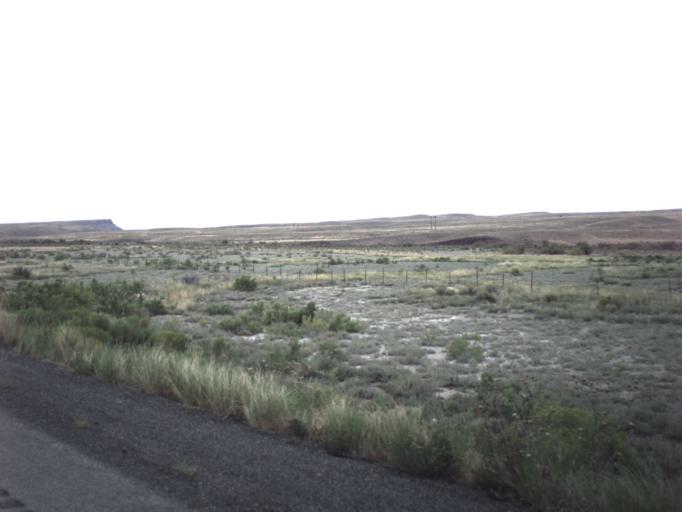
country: US
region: Utah
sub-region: Carbon County
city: East Carbon City
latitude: 39.4645
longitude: -110.4915
